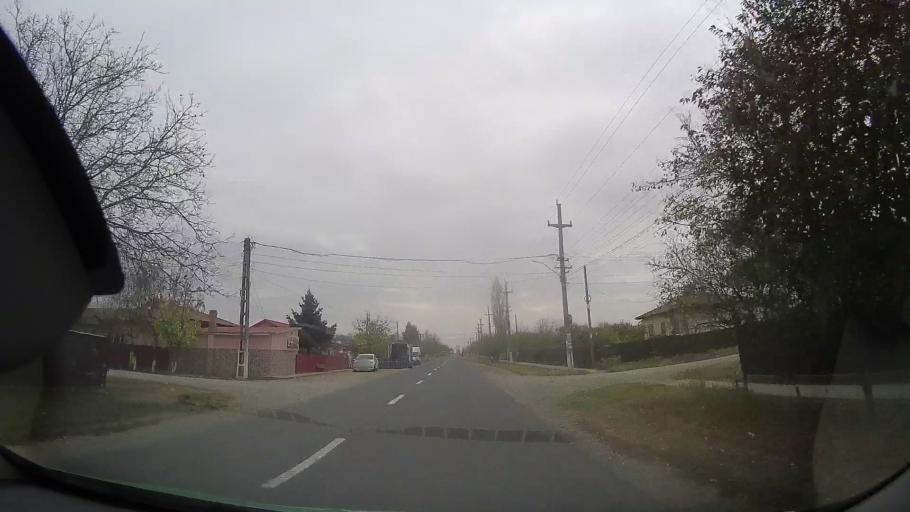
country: RO
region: Ialomita
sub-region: Comuna Garbovi
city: Garbovi
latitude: 44.7840
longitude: 26.7588
